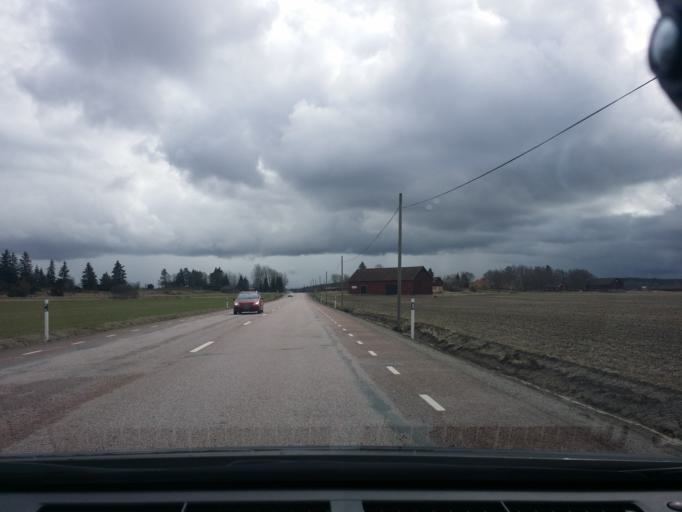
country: SE
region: Uppsala
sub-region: Enkopings Kommun
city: Irsta
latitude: 59.7801
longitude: 16.8498
